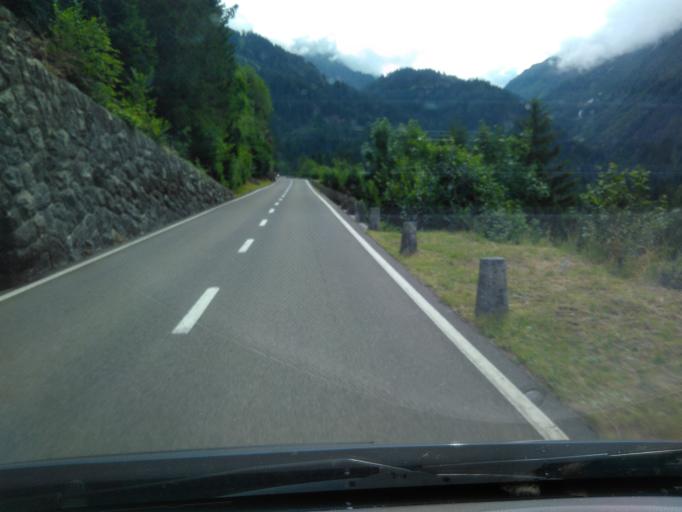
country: CH
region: Obwalden
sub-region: Obwalden
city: Engelberg
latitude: 46.7391
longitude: 8.3671
